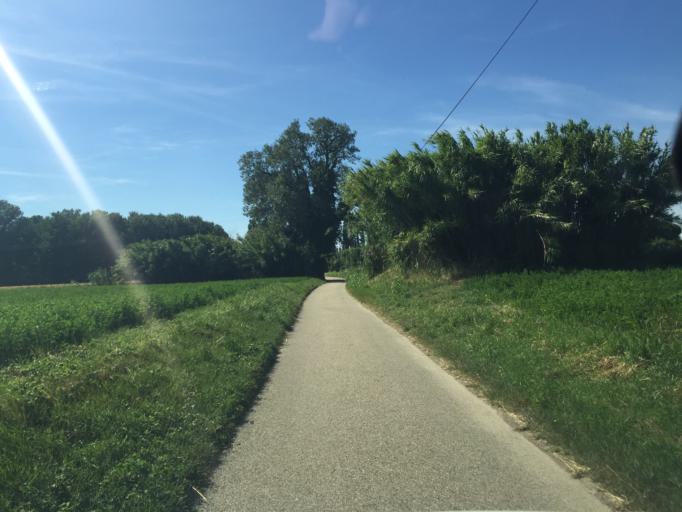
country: FR
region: Provence-Alpes-Cote d'Azur
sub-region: Departement du Vaucluse
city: Caderousse
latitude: 44.0892
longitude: 4.7666
